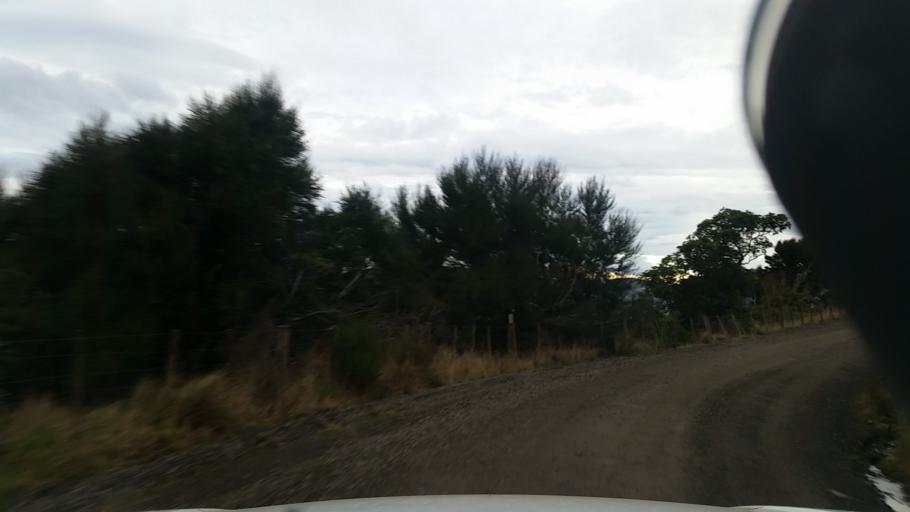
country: NZ
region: Canterbury
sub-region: Christchurch City
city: Christchurch
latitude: -43.8354
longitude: 172.9714
